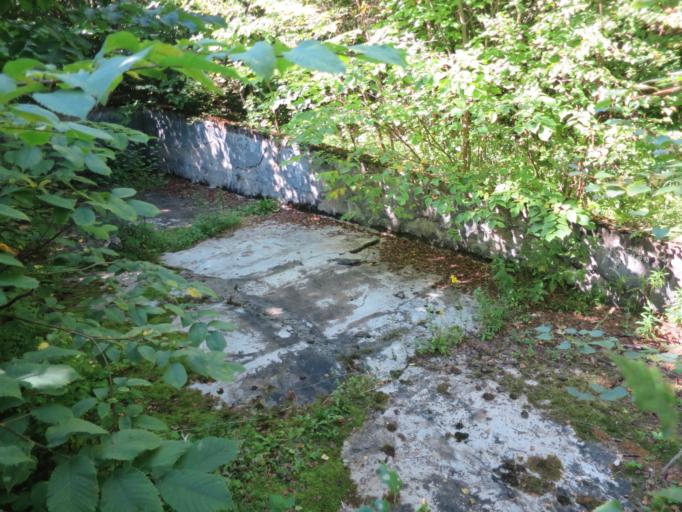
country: LV
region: Sigulda
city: Sigulda
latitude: 57.1082
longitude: 24.8108
